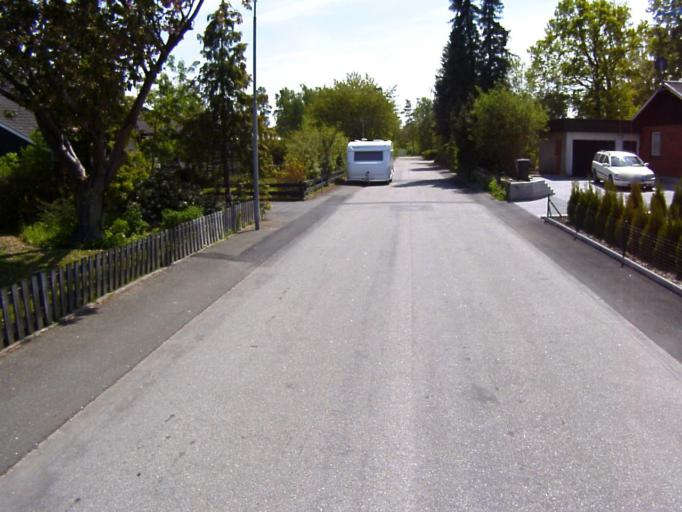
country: SE
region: Skane
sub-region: Kristianstads Kommun
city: Kristianstad
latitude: 56.0718
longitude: 14.0916
